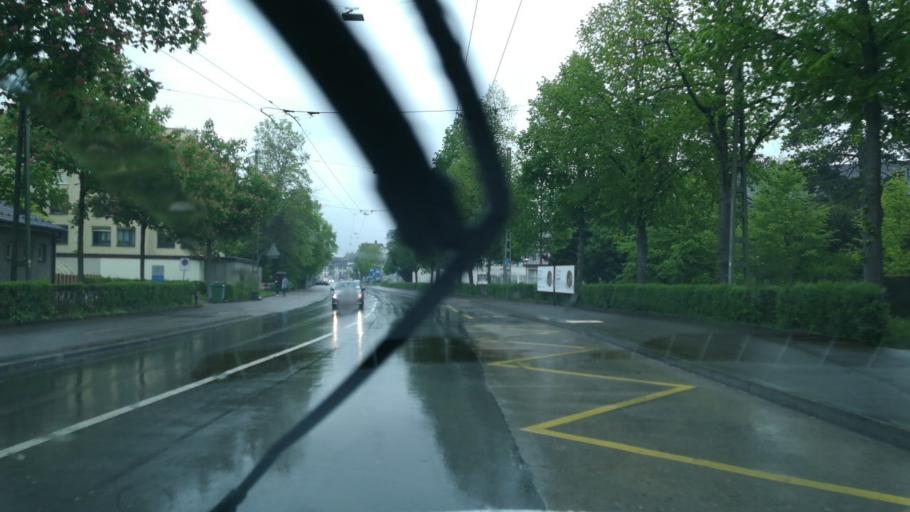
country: CH
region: Zurich
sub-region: Bezirk Winterthur
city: Mattenbach (Kreis 7) / Deutweg
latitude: 47.4956
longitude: 8.7371
